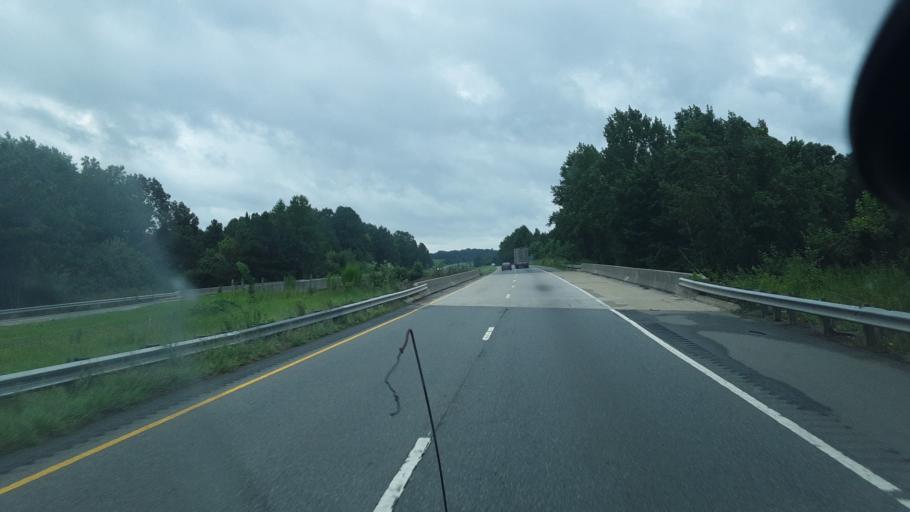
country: US
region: North Carolina
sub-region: Montgomery County
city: Biscoe
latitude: 35.5035
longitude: -79.7814
